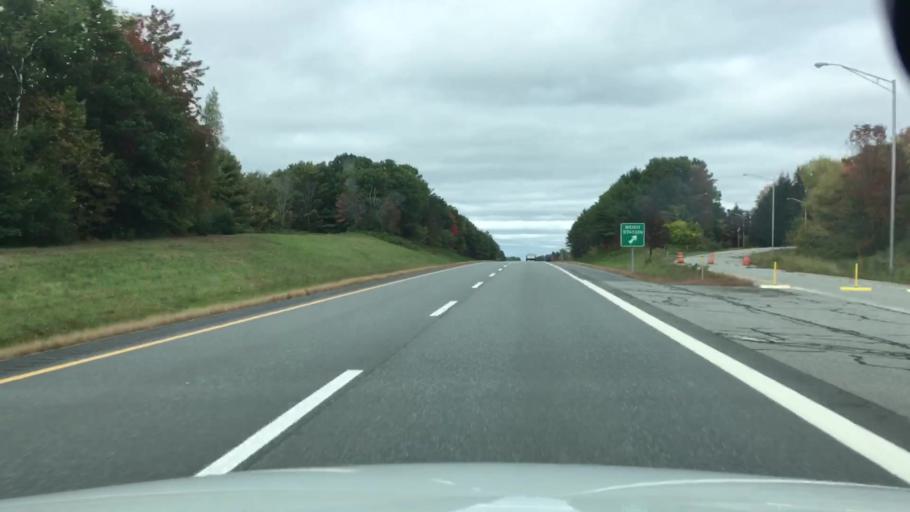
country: US
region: Maine
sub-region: Waldo County
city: Burnham
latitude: 44.7441
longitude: -69.4265
